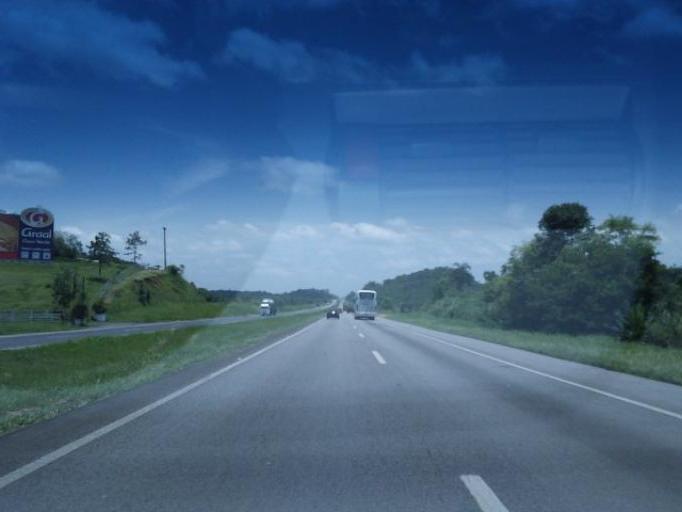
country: BR
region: Sao Paulo
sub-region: Registro
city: Registro
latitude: -24.4289
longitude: -47.7849
